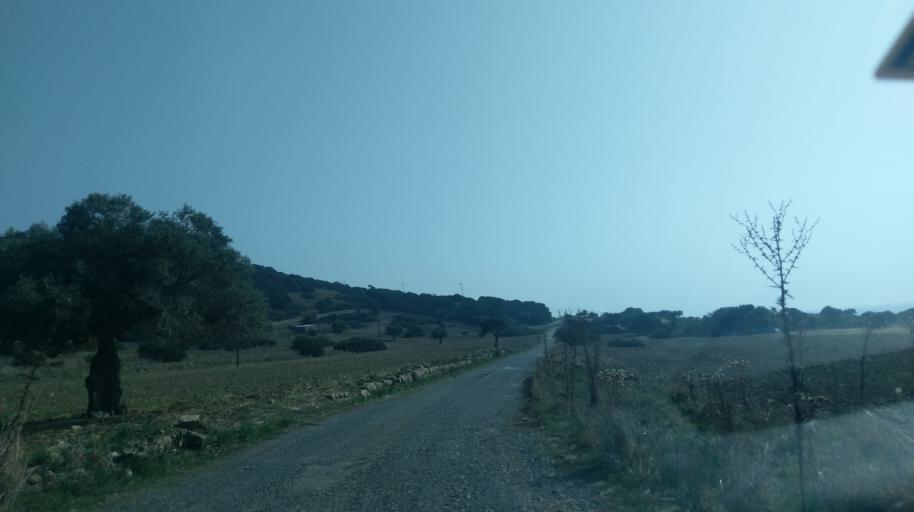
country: CY
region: Ammochostos
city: Rizokarpaso
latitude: 35.6485
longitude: 34.5522
